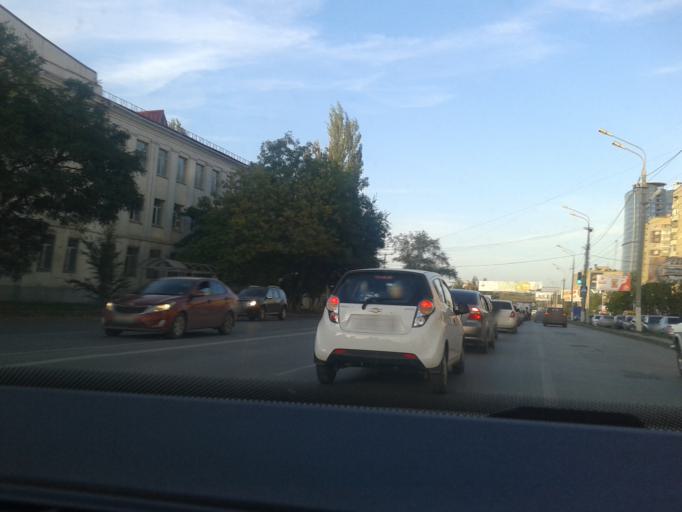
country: RU
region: Volgograd
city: Volgograd
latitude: 48.7269
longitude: 44.5187
